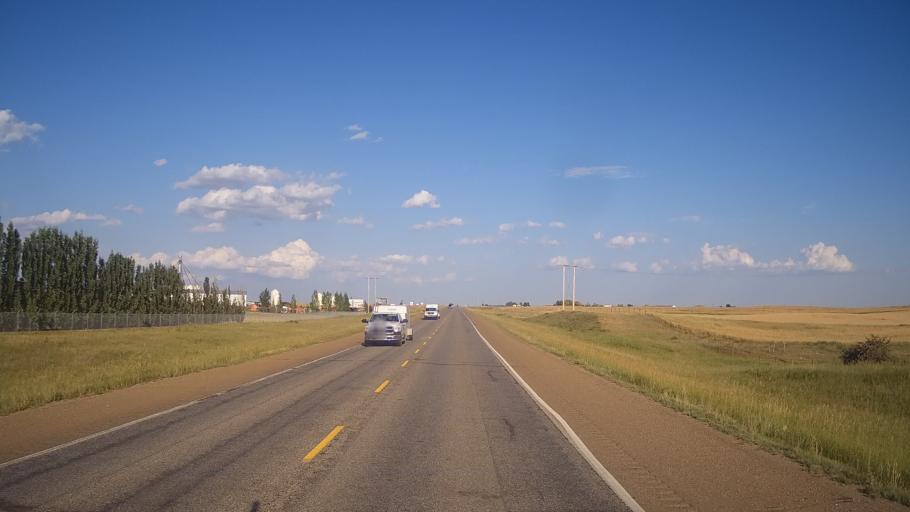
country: CA
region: Alberta
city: Hanna
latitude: 51.6331
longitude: -111.9344
